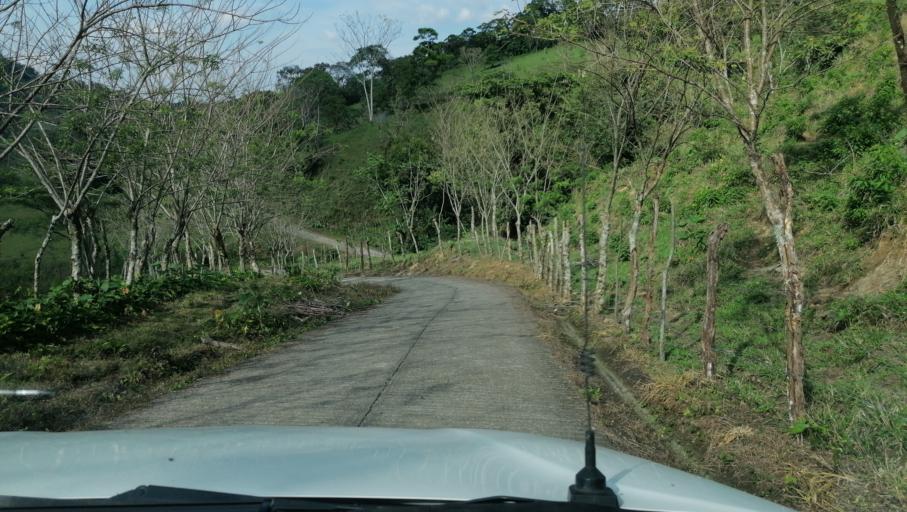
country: MX
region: Chiapas
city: Ostuacan
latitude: 17.4671
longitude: -93.2368
